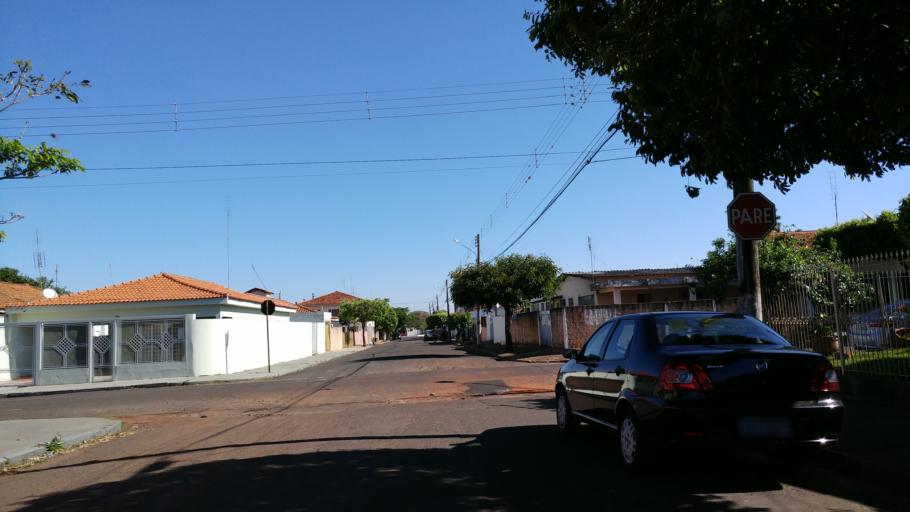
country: BR
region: Sao Paulo
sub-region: Paraguacu Paulista
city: Paraguacu Paulista
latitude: -22.4162
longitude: -50.5805
